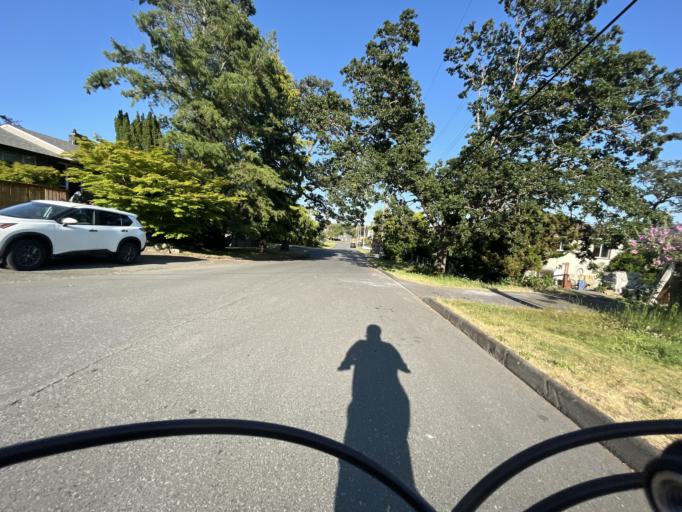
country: CA
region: British Columbia
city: Victoria
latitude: 48.4381
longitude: -123.3416
